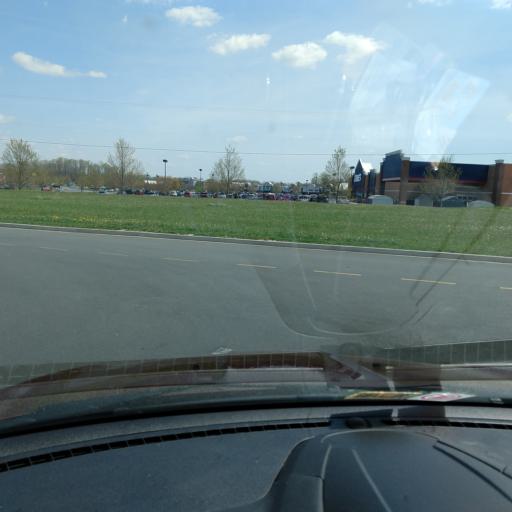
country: US
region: West Virginia
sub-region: Fayette County
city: Fayetteville
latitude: 38.0304
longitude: -81.1223
